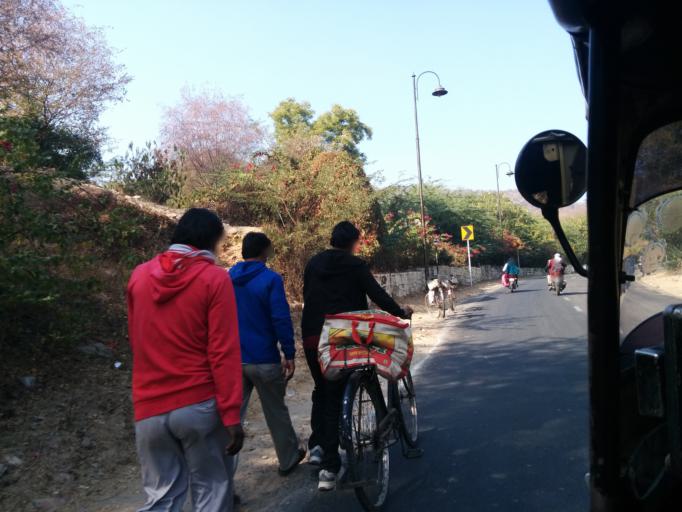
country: IN
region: Rajasthan
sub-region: Jaipur
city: Jaipur
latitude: 26.9653
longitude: 75.8466
